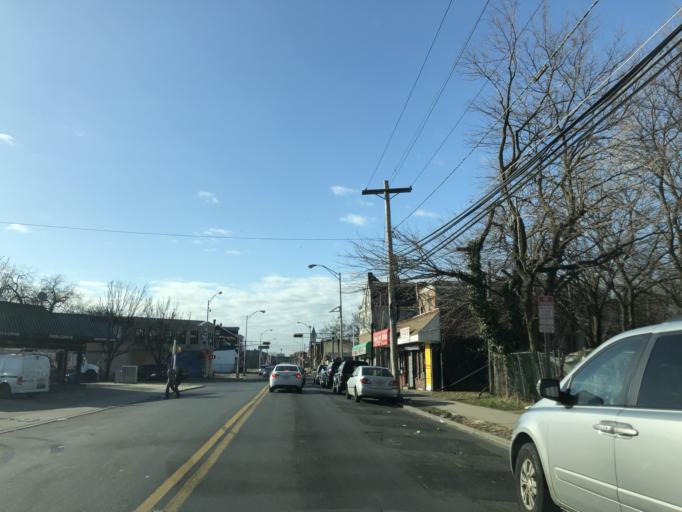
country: US
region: New Jersey
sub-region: Camden County
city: Wood-Lynne
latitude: 39.9322
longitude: -75.1018
